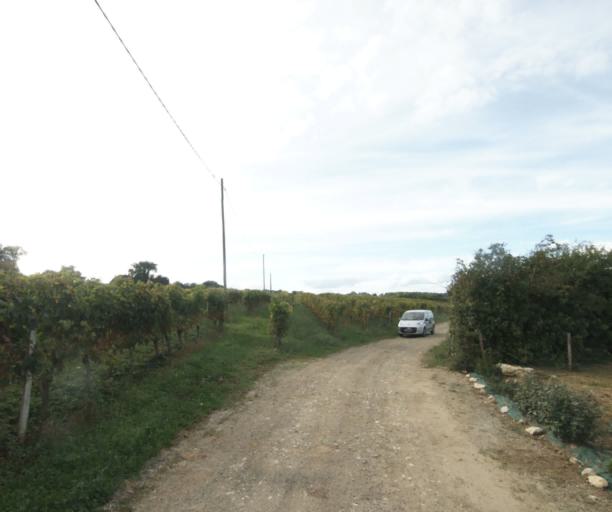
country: FR
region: Midi-Pyrenees
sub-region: Departement du Gers
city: Gondrin
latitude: 43.8736
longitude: 0.2499
